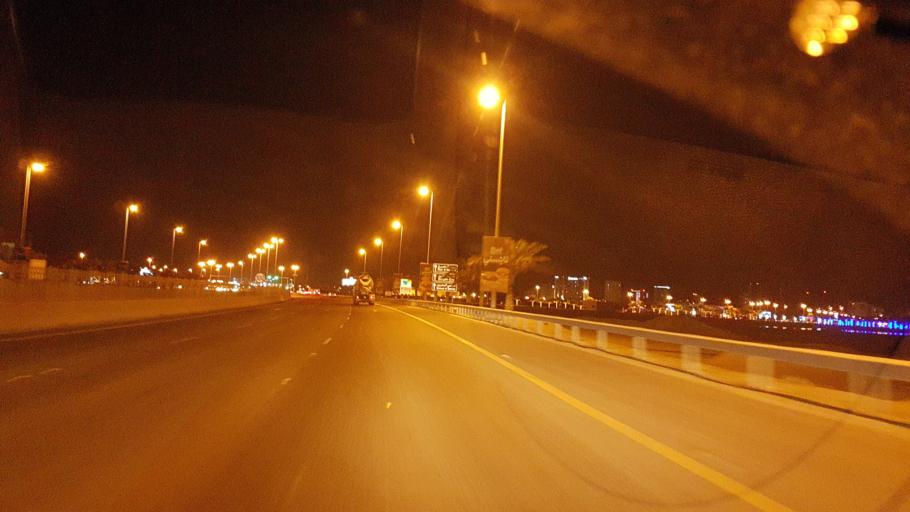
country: BH
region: Muharraq
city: Al Hadd
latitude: 26.2720
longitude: 50.6614
